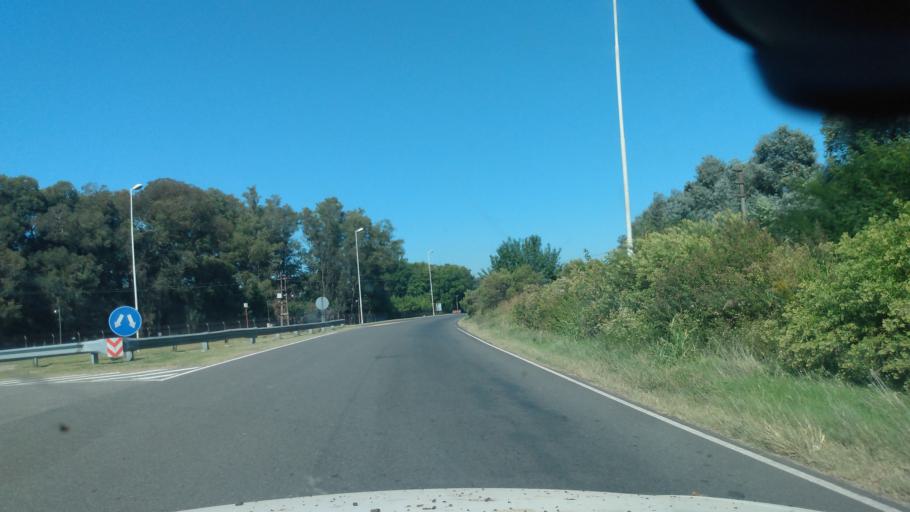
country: AR
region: Buenos Aires
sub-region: Partido de Lujan
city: Lujan
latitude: -34.5087
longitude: -59.0942
